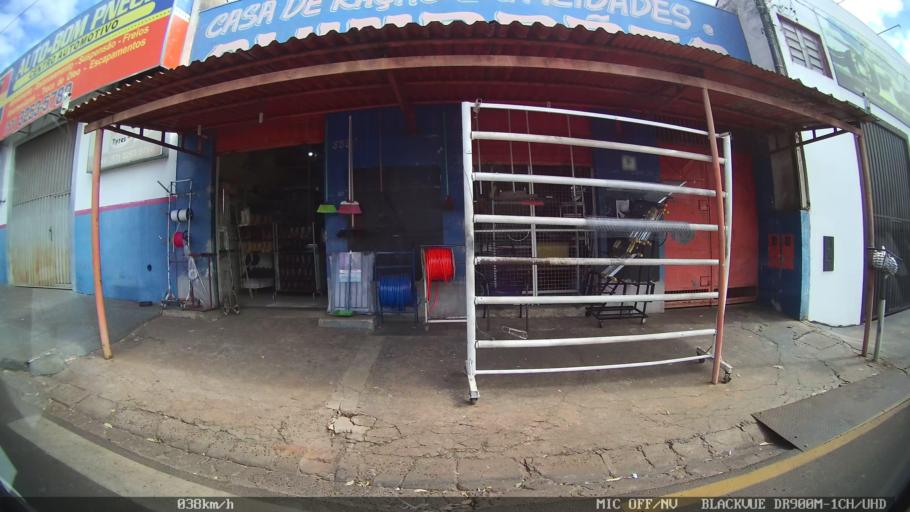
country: BR
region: Sao Paulo
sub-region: Sao Jose Do Rio Preto
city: Sao Jose do Rio Preto
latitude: -20.8052
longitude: -49.5056
